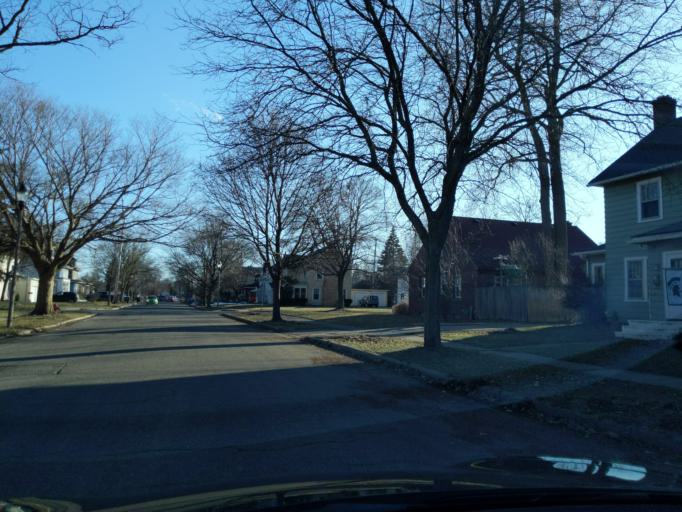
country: US
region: Michigan
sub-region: Ingham County
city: Lansing
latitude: 42.7281
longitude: -84.5727
